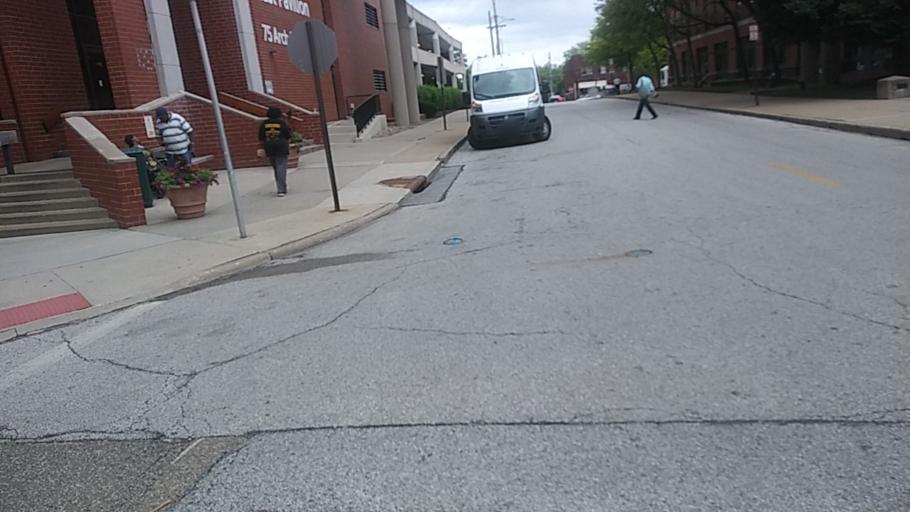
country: US
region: Ohio
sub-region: Summit County
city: Akron
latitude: 41.0801
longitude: -81.4998
